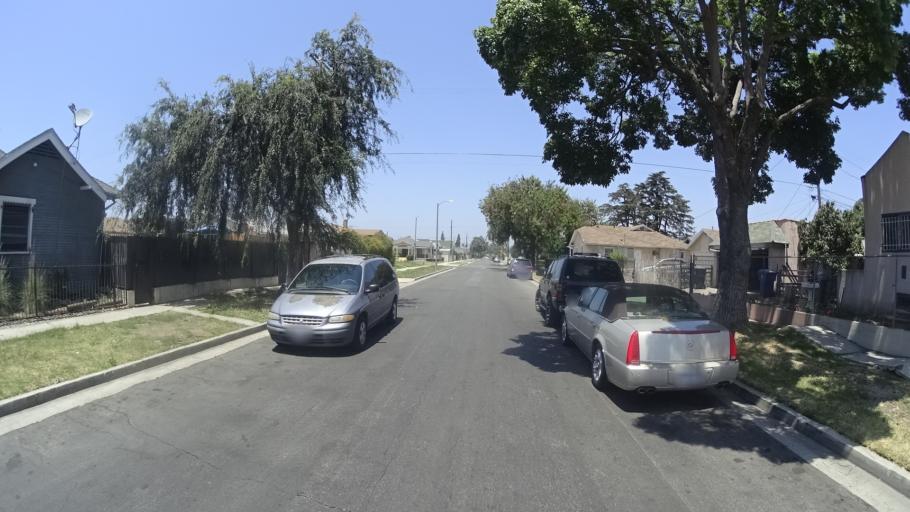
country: US
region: California
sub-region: Los Angeles County
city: View Park-Windsor Hills
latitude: 34.0065
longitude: -118.3113
